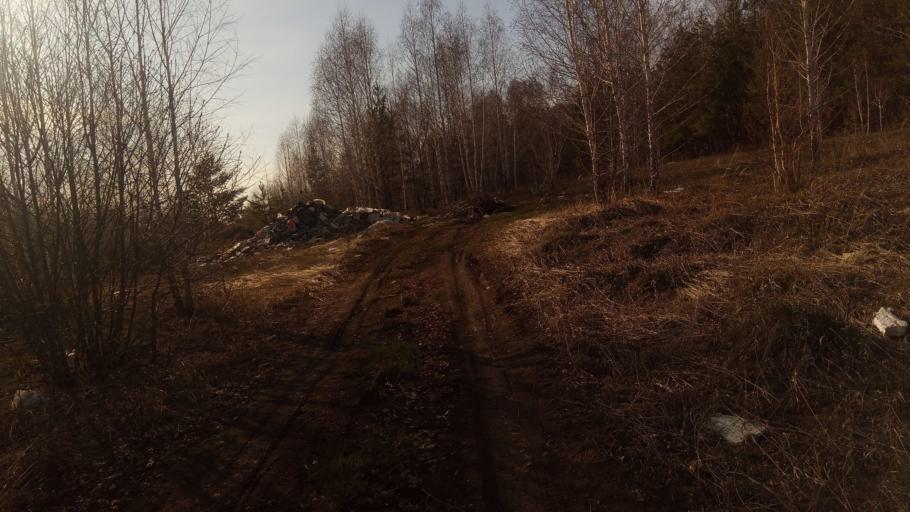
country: RU
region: Chelyabinsk
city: Sargazy
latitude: 55.1190
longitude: 61.2523
